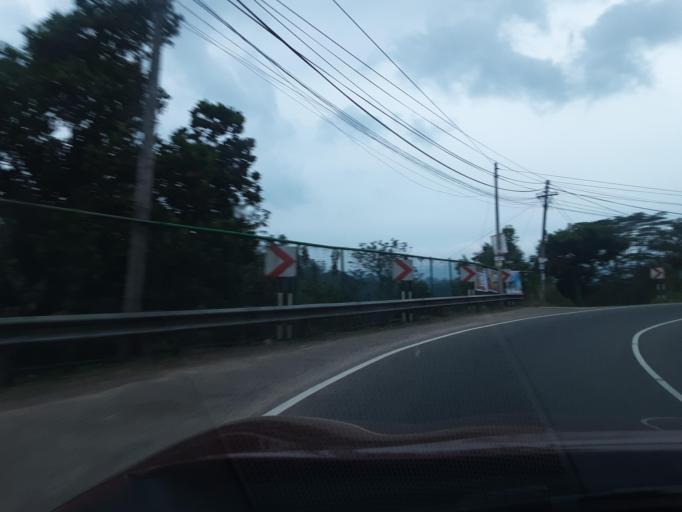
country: LK
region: Central
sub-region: Nuwara Eliya District
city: Nuwara Eliya
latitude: 6.9003
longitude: 80.9055
